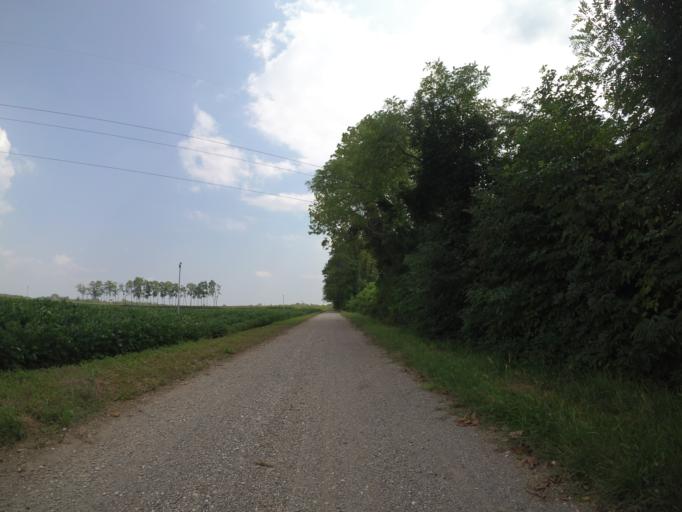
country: IT
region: Friuli Venezia Giulia
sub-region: Provincia di Udine
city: Codroipo
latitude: 45.9828
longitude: 13.0007
